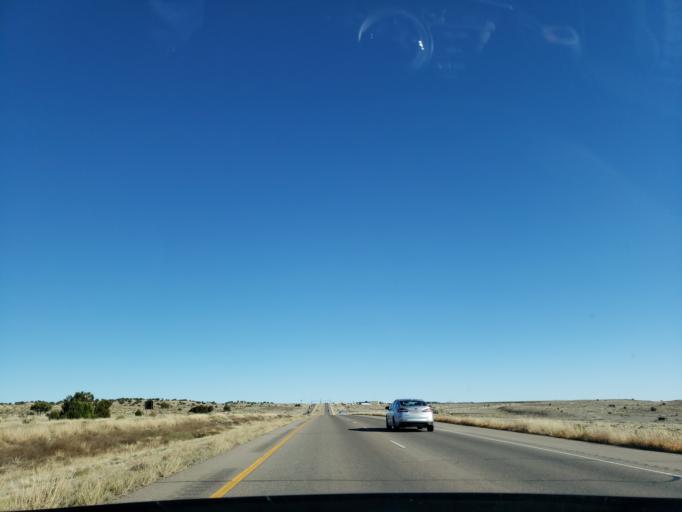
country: US
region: Colorado
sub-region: Fremont County
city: Florence
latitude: 38.4409
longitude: -105.1284
